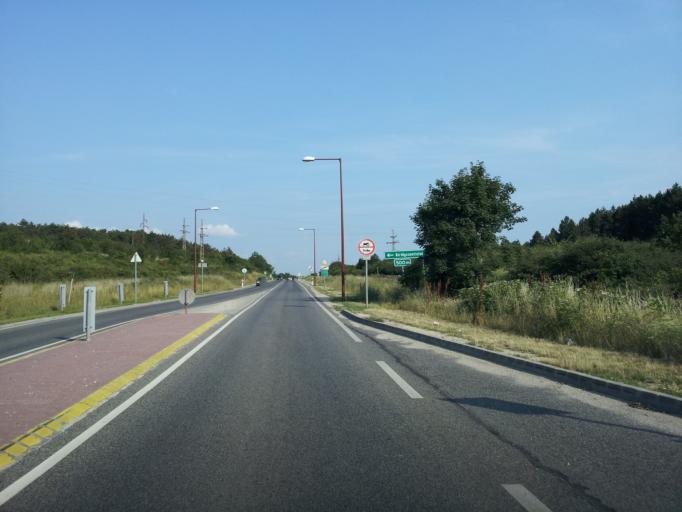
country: HU
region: Veszprem
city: Liter
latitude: 47.0967
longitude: 18.0192
